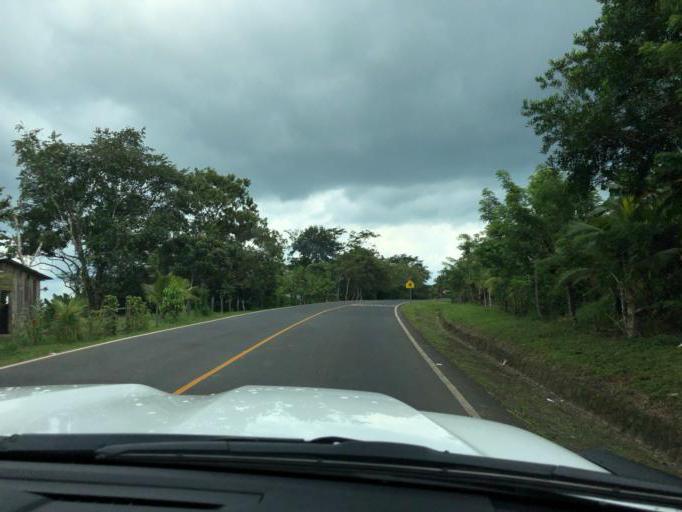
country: NI
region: Chontales
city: Villa Sandino
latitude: 11.9987
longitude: -84.8355
